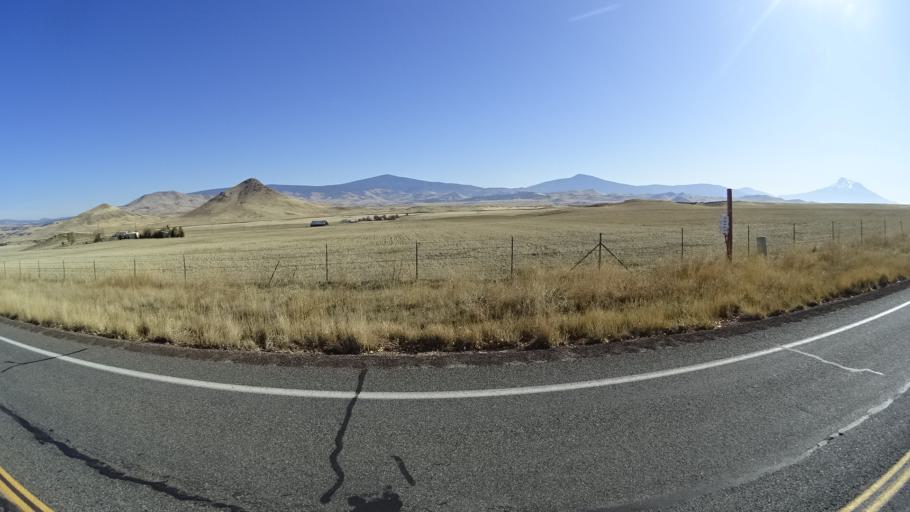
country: US
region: California
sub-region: Siskiyou County
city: Montague
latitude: 41.8137
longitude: -122.4982
